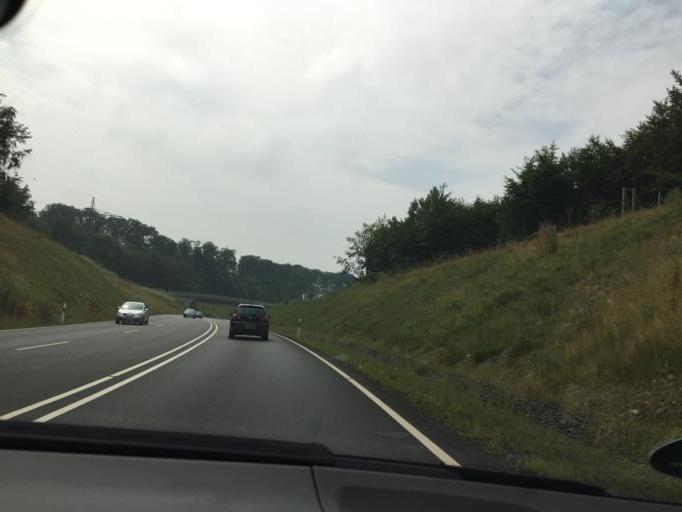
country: DE
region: Rheinland-Pfalz
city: Rengsdorf
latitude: 50.5076
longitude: 7.4807
